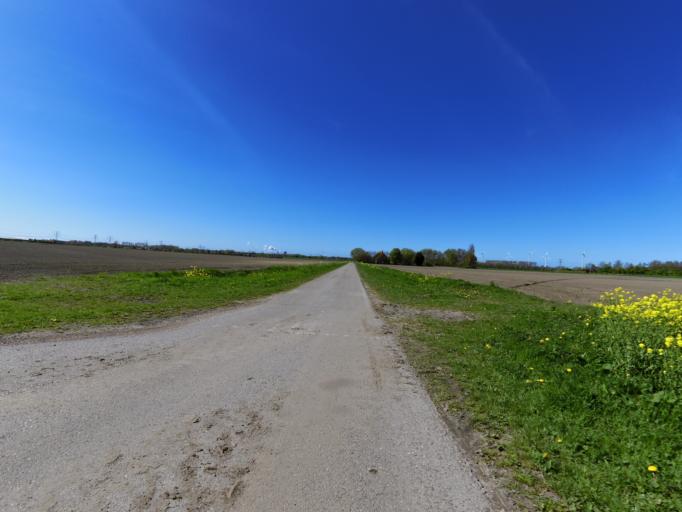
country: NL
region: South Holland
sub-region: Gemeente Brielle
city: Brielle
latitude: 51.9148
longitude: 4.1447
